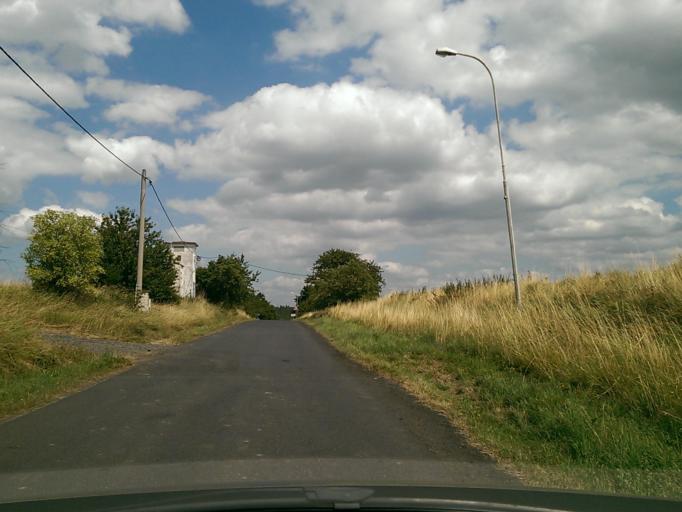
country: CZ
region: Ustecky
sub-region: Okres Litomerice
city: Steti
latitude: 50.5116
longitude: 14.4182
